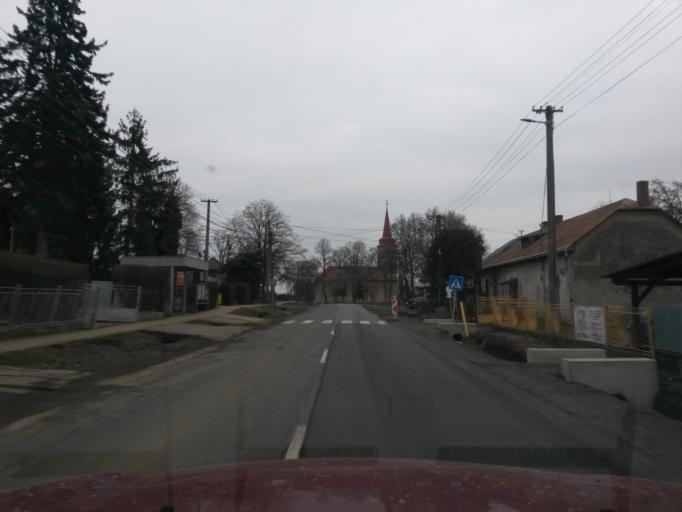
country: SK
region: Kosicky
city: Trebisov
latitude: 48.6824
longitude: 21.8143
